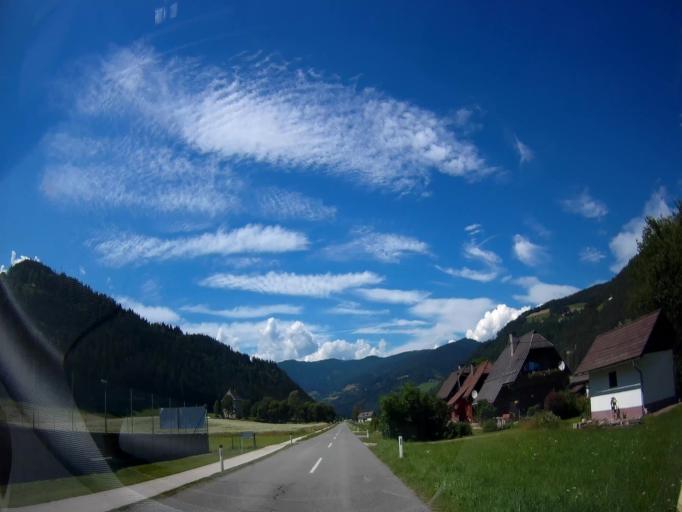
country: AT
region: Carinthia
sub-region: Politischer Bezirk Sankt Veit an der Glan
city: Glodnitz
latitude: 46.8775
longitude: 14.1164
